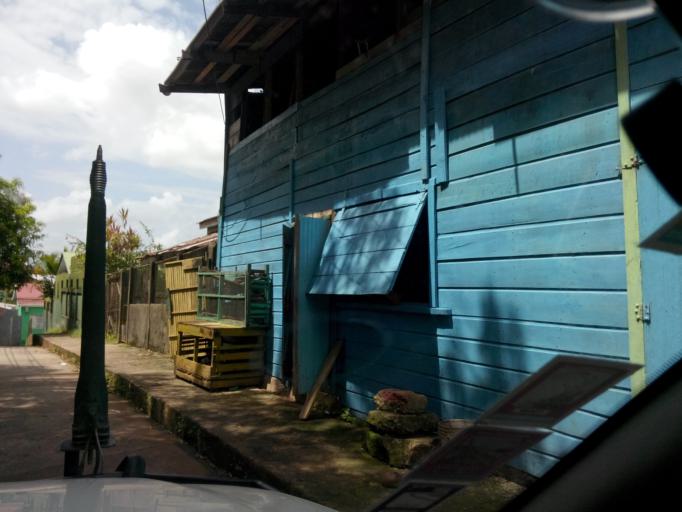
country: NI
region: Atlantico Sur
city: Bluefields
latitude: 12.0143
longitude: -83.7601
